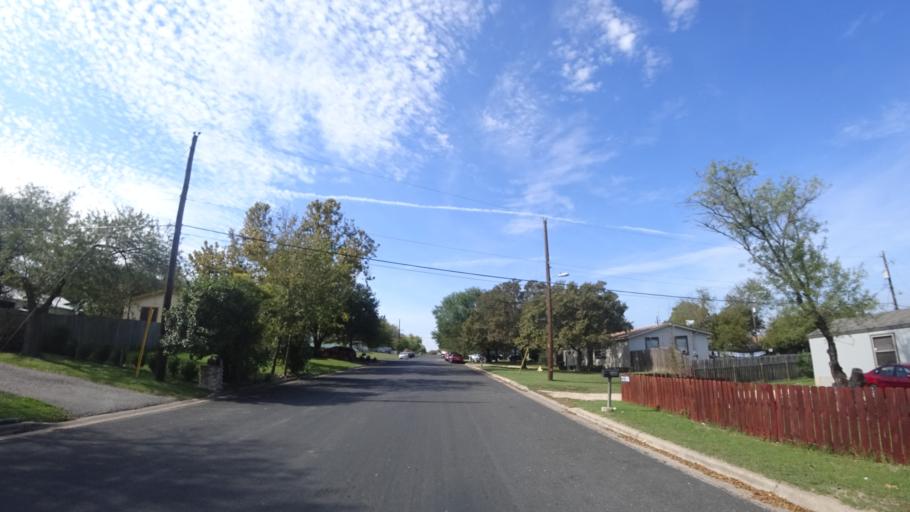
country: US
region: Texas
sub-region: Travis County
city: Pflugerville
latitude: 30.4102
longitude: -97.6267
